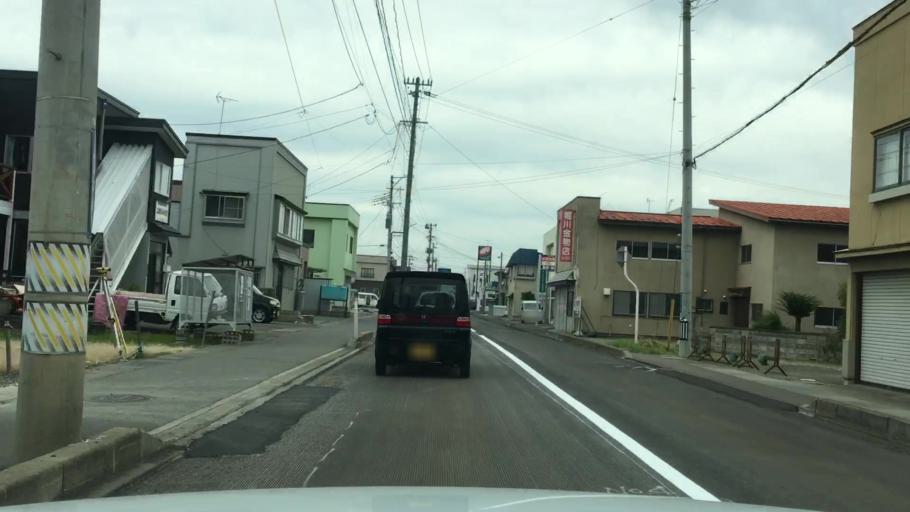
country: JP
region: Aomori
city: Hirosaki
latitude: 40.6270
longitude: 140.4547
